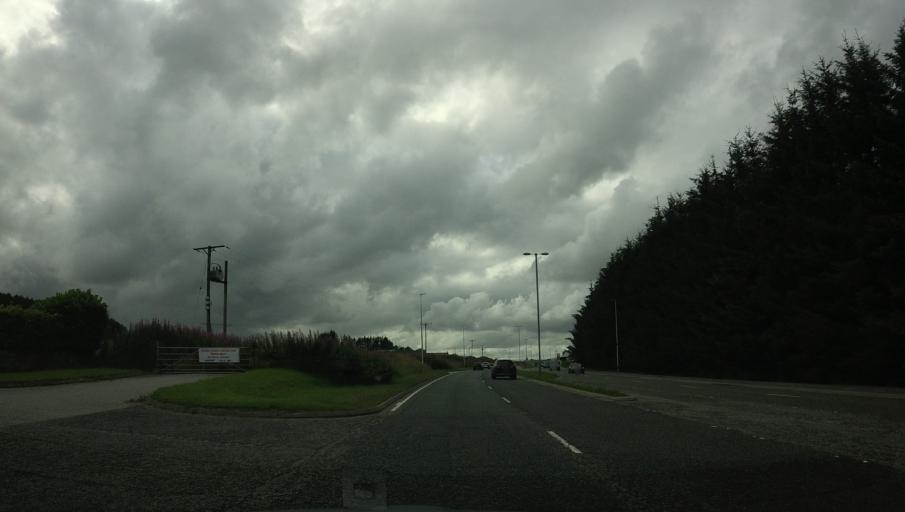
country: GB
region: Scotland
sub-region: Aberdeenshire
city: Westhill
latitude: 57.1462
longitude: -2.2339
